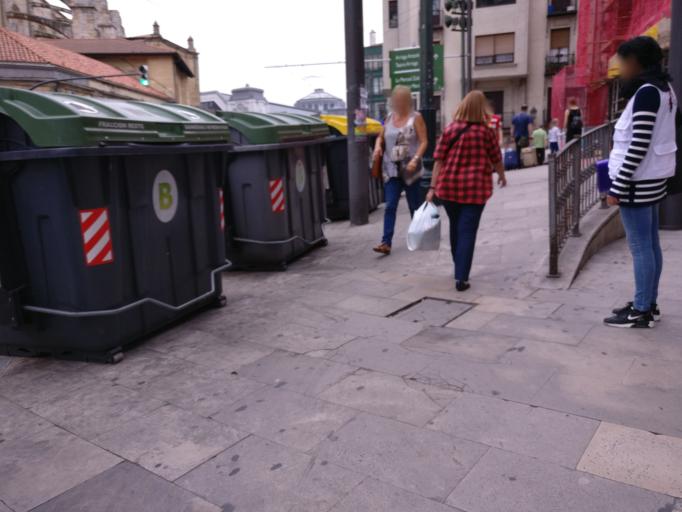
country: ES
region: Basque Country
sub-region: Bizkaia
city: Santutxu
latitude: 43.2555
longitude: -2.9226
